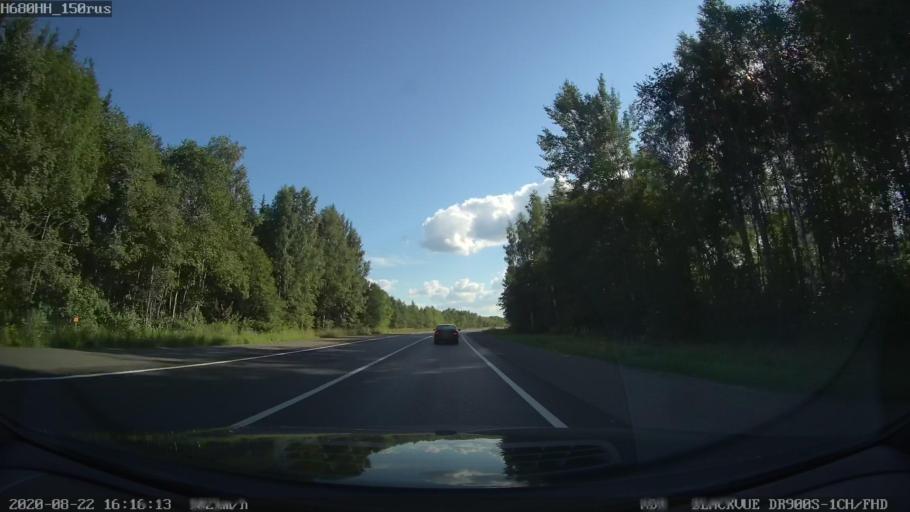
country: RU
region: Tverskaya
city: Rameshki
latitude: 57.4371
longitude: 36.1824
